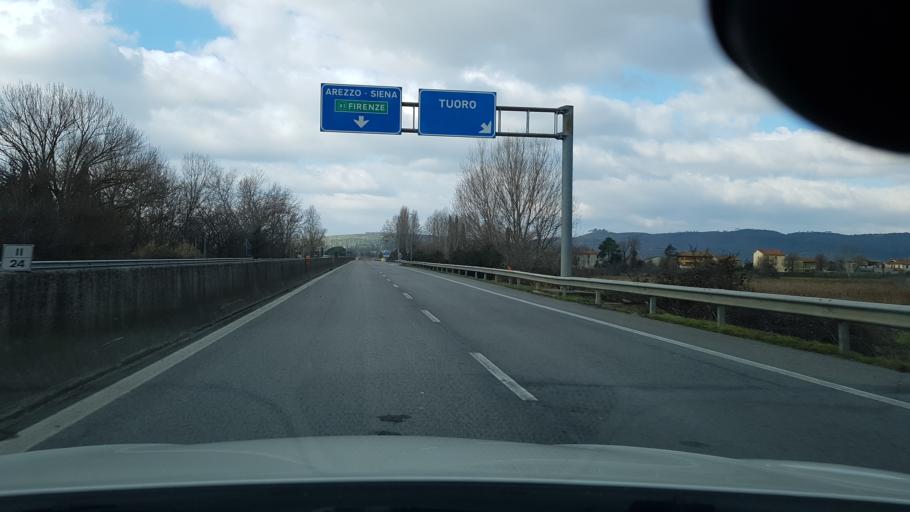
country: IT
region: Umbria
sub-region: Provincia di Perugia
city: Tuoro sul Trasimeno
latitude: 43.1976
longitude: 12.0815
